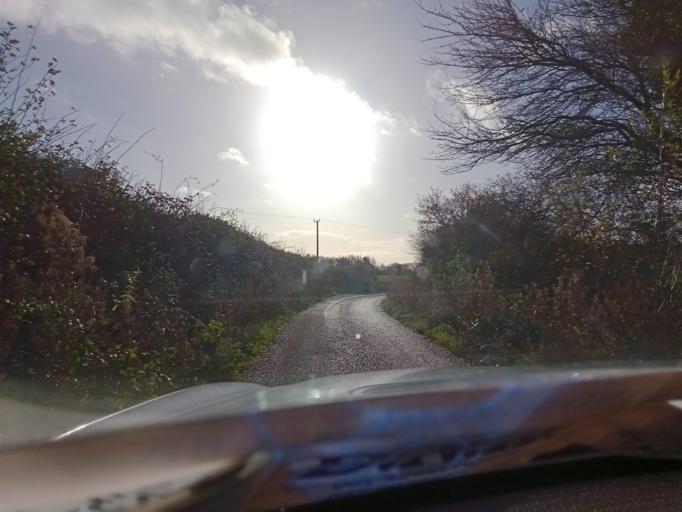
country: IE
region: Leinster
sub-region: Kilkenny
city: Mooncoin
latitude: 52.3096
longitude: -7.2762
